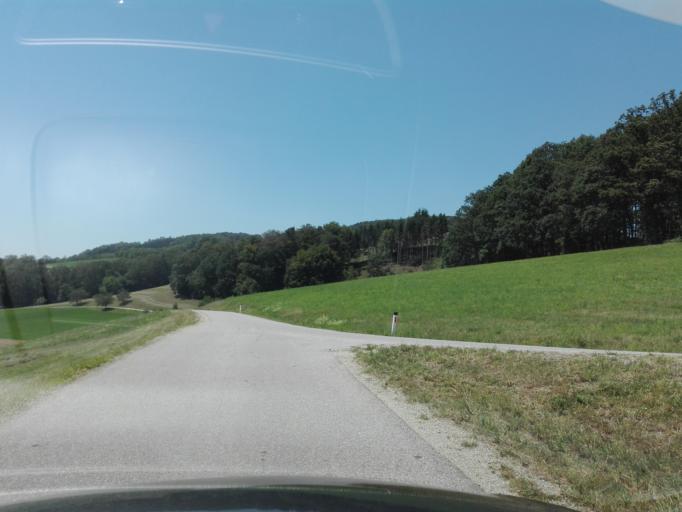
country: AT
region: Upper Austria
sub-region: Politischer Bezirk Urfahr-Umgebung
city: Engerwitzdorf
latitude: 48.2946
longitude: 14.4341
